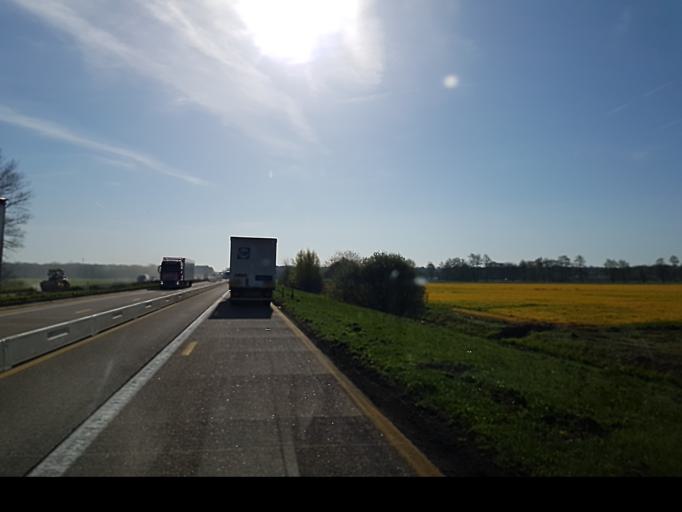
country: BE
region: Flanders
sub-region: Provincie Antwerpen
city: Oud-Turnhout
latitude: 51.2964
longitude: 4.9938
